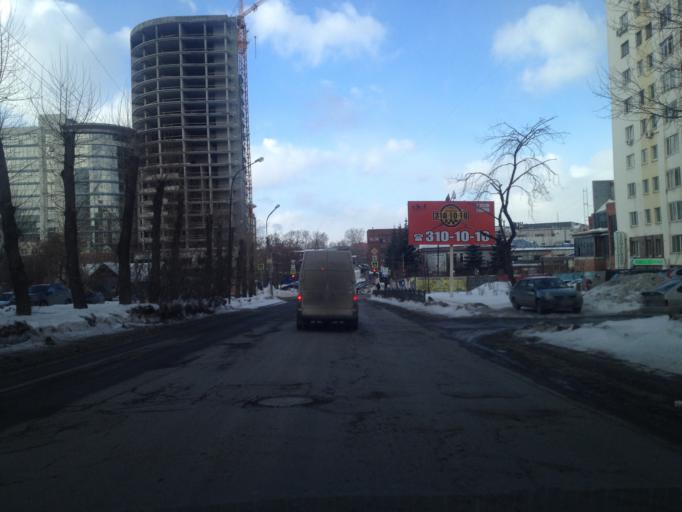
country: RU
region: Sverdlovsk
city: Yekaterinburg
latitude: 56.8629
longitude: 60.6225
